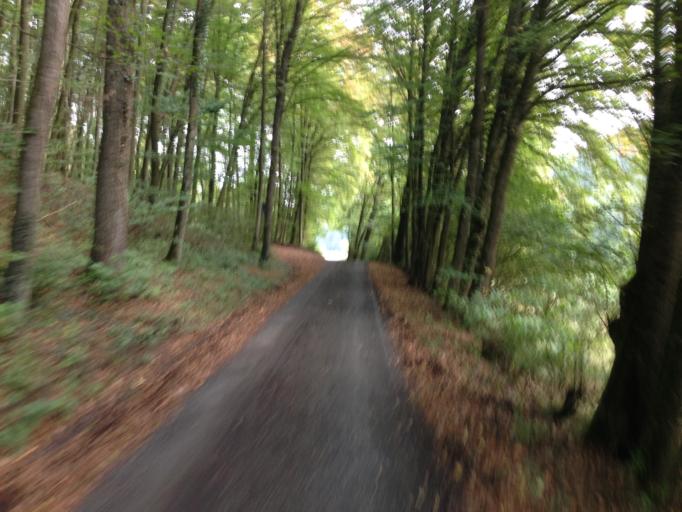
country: DE
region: Hesse
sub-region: Regierungsbezirk Giessen
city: Heuchelheim
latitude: 50.6455
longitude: 8.5619
